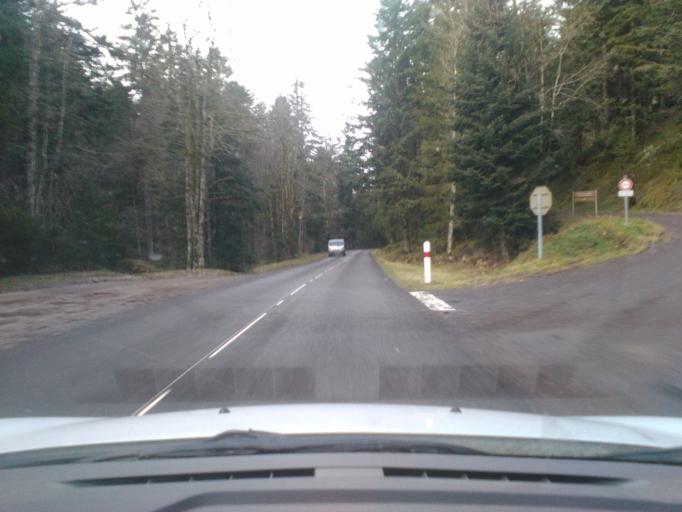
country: FR
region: Lorraine
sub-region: Departement des Vosges
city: Xonrupt-Longemer
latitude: 48.1057
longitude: 6.9730
